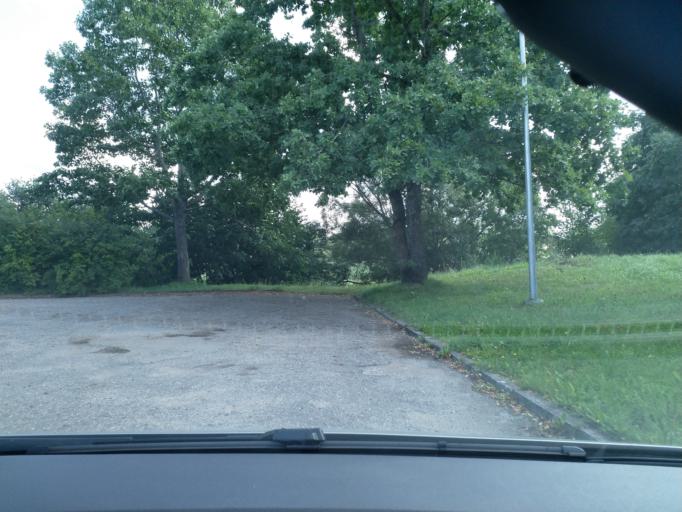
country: LV
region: Kuldigas Rajons
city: Kuldiga
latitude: 56.9771
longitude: 21.9689
